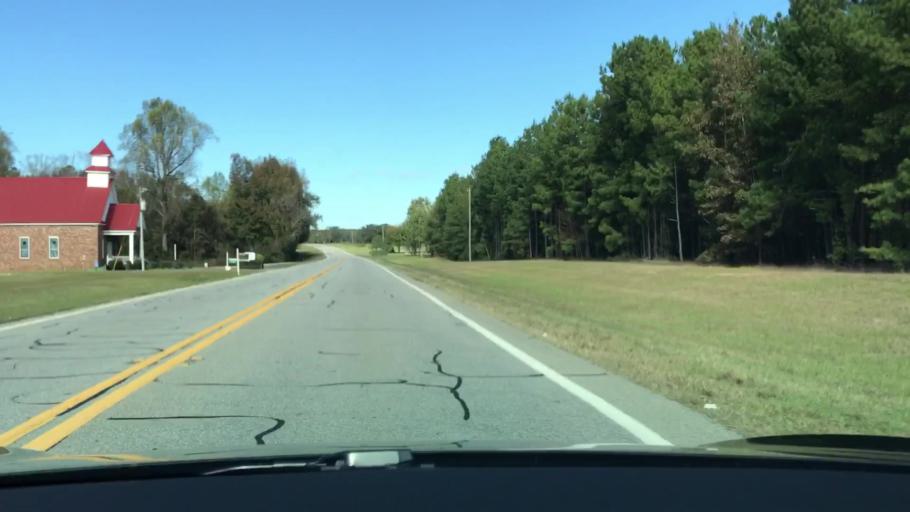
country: US
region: Georgia
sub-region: Glascock County
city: Gibson
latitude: 33.3386
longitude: -82.5719
